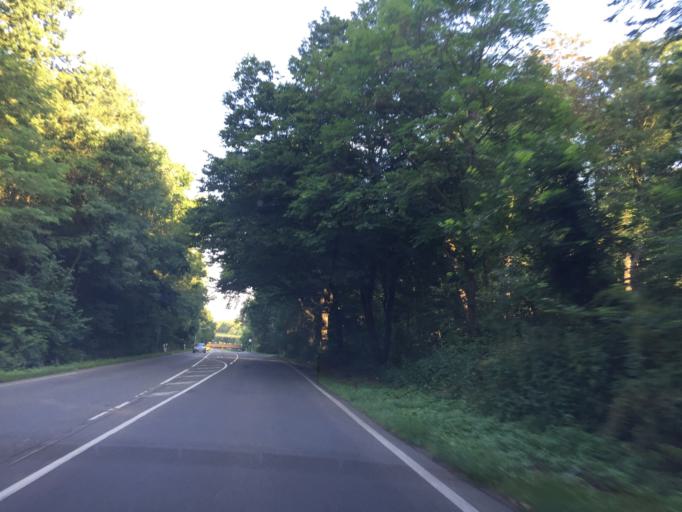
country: DE
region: North Rhine-Westphalia
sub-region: Regierungsbezirk Koln
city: Neustadt/Sued
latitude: 50.9009
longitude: 6.9194
